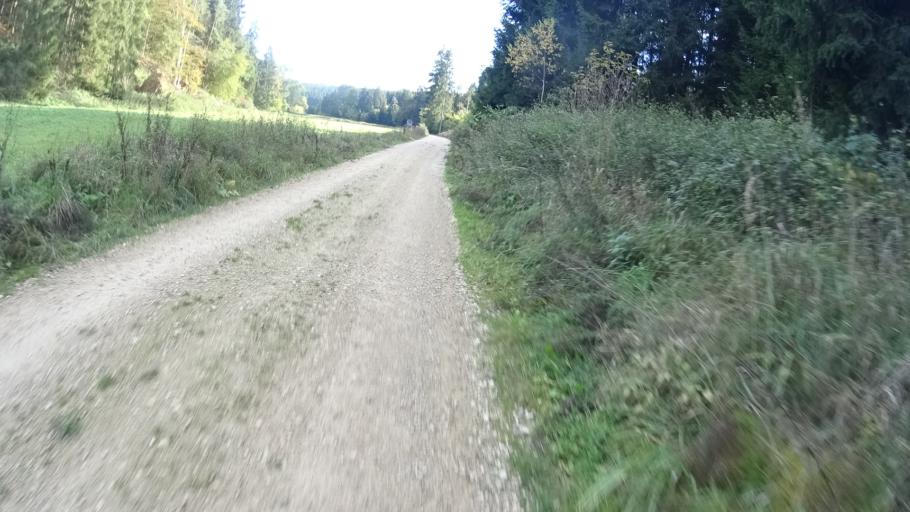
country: DE
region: Bavaria
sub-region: Upper Bavaria
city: Bohmfeld
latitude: 48.8852
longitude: 11.3514
